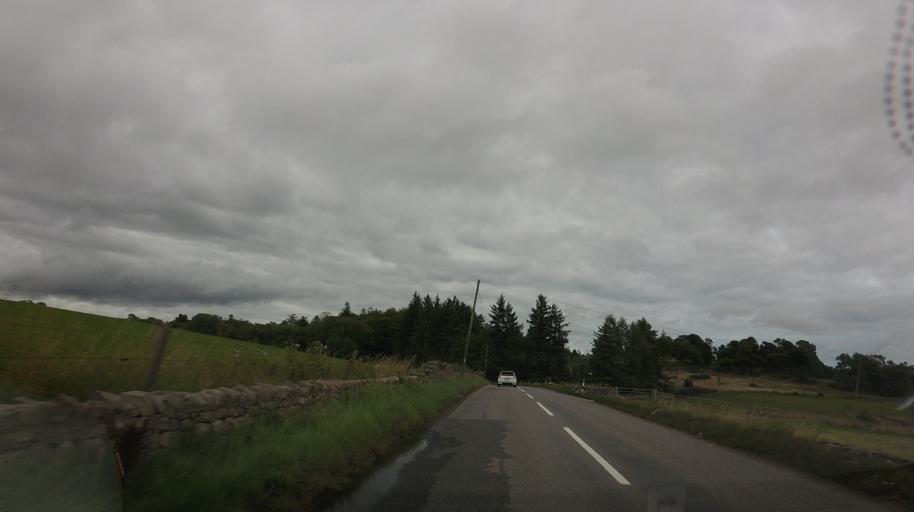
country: GB
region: Scotland
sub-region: Aberdeenshire
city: Kemnay
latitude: 57.1541
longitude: -2.4319
